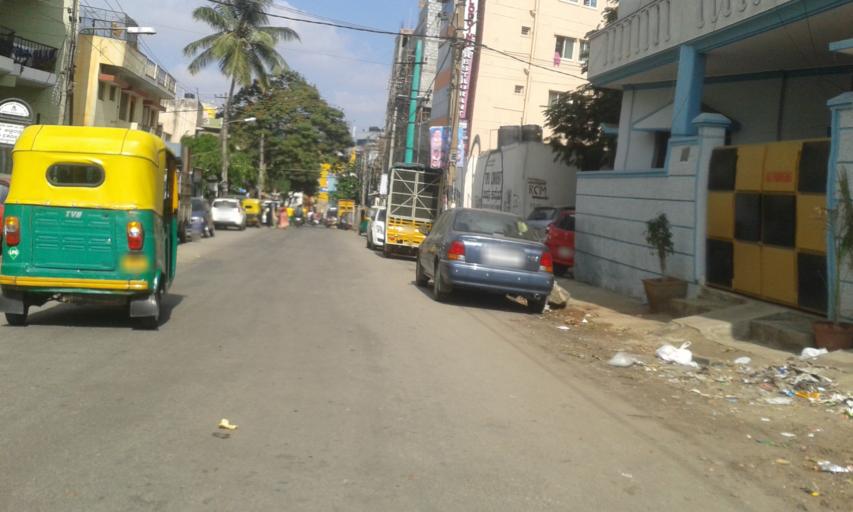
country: IN
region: Karnataka
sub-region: Bangalore Urban
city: Bangalore
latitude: 12.9409
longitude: 77.5929
